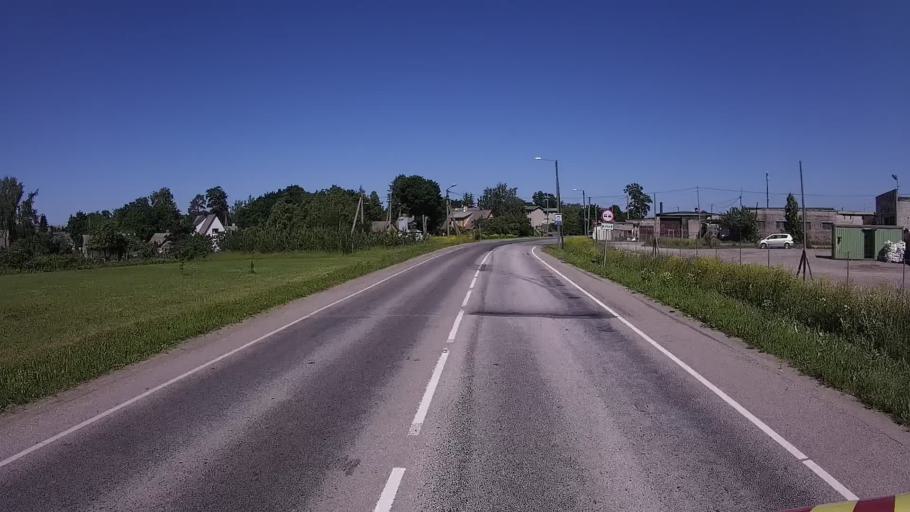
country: EE
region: Ida-Virumaa
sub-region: Johvi vald
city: Johvi
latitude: 59.3326
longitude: 27.3792
